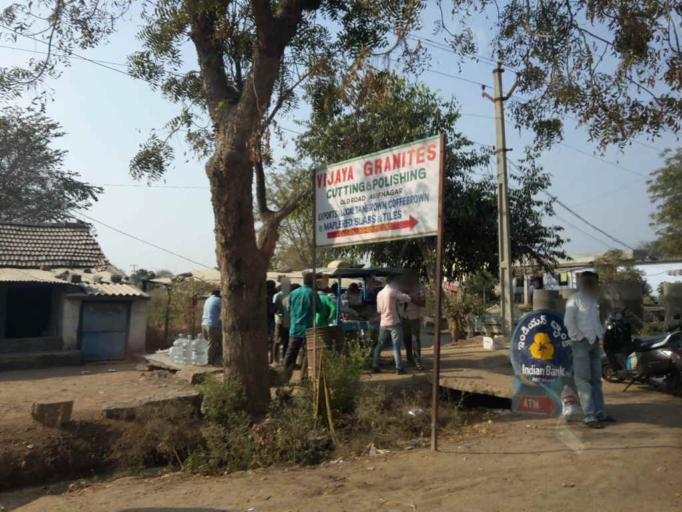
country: IN
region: Telangana
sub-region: Karimnagar
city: Kottapalli
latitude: 18.4316
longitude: 79.0164
